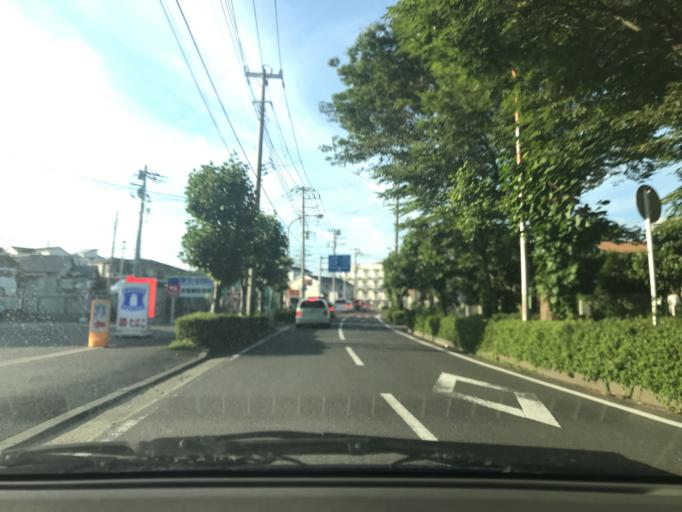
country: JP
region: Kanagawa
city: Fujisawa
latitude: 35.3457
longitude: 139.4617
